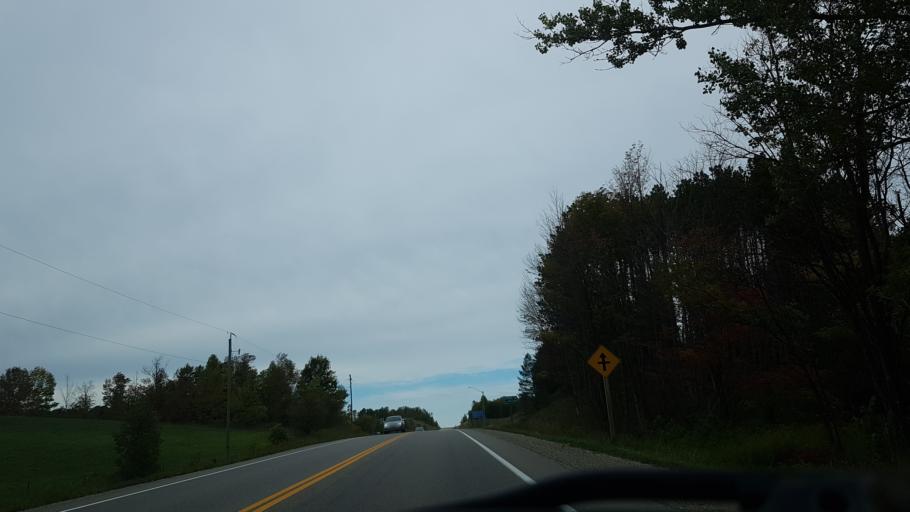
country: CA
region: Ontario
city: Orangeville
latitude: 44.0516
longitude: -80.0117
